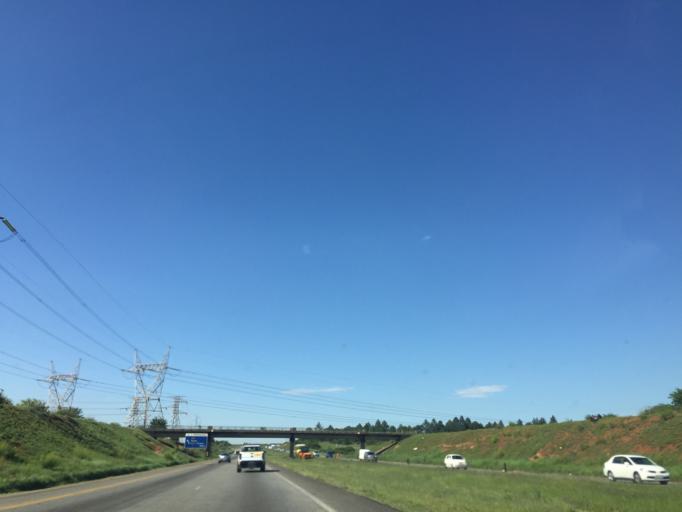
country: ZA
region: Gauteng
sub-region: Sedibeng District Municipality
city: Meyerton
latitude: -26.6170
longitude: 27.9739
